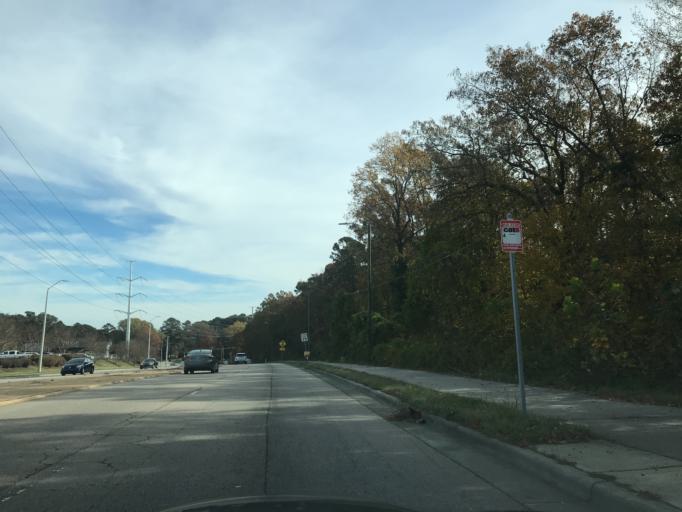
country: US
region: North Carolina
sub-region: Wake County
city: West Raleigh
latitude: 35.8018
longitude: -78.6875
